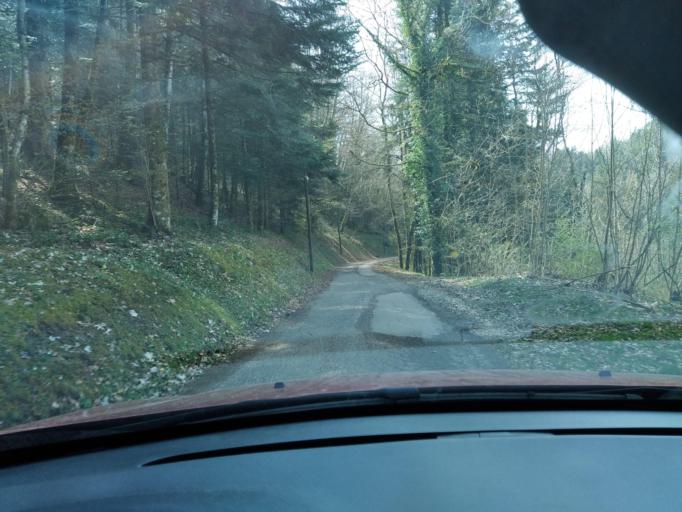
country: FR
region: Franche-Comte
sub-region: Departement du Jura
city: Lavans-les-Saint-Claude
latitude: 46.3974
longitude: 5.7463
